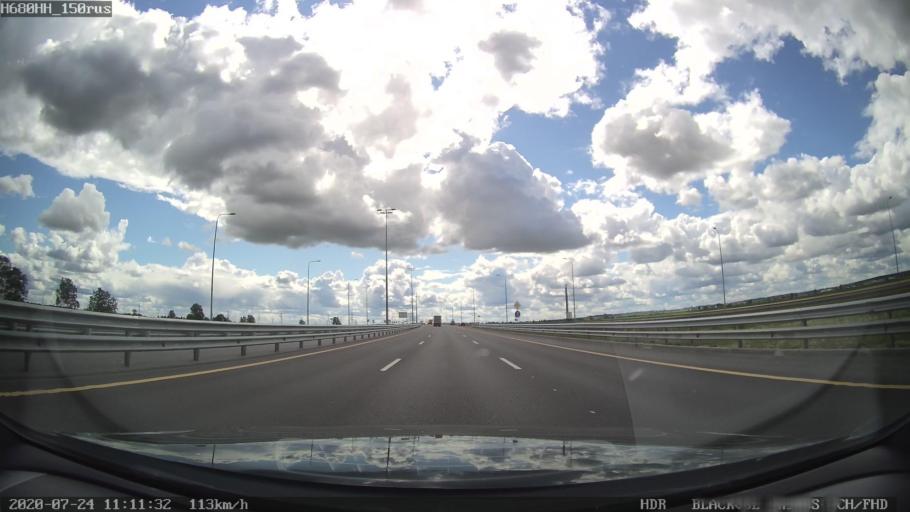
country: RU
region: Leningrad
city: Fedorovskoye
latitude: 59.7213
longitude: 30.5169
